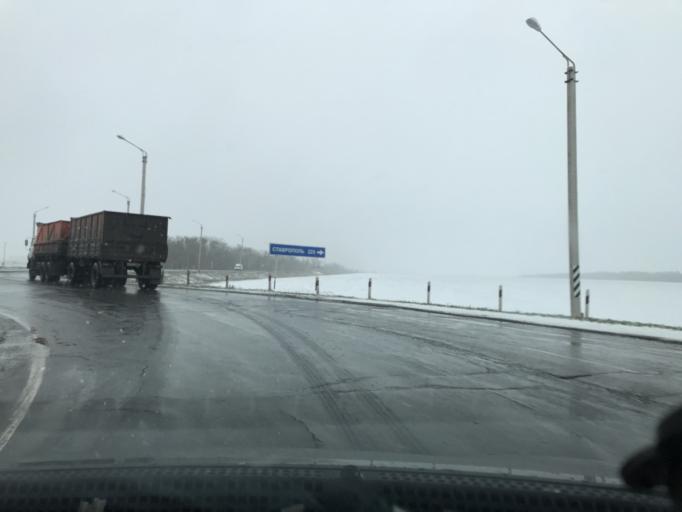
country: RU
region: Rostov
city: Yegorlykskaya
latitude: 46.5864
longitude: 40.6316
